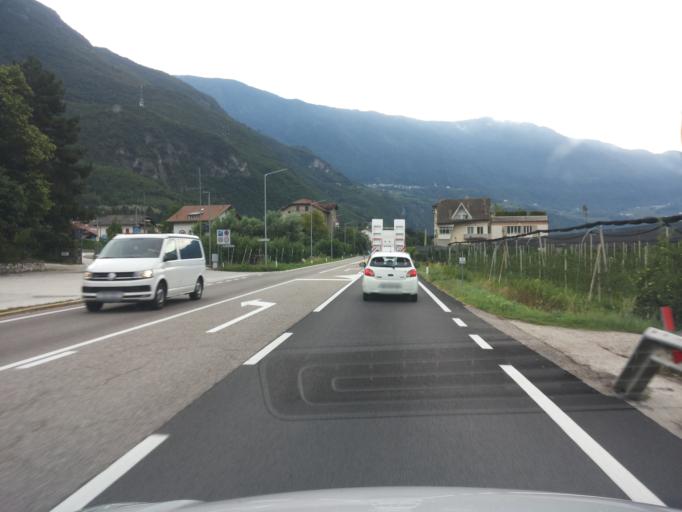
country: IT
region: Trentino-Alto Adige
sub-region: Bolzano
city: Laghetti
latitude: 46.2772
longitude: 11.2389
